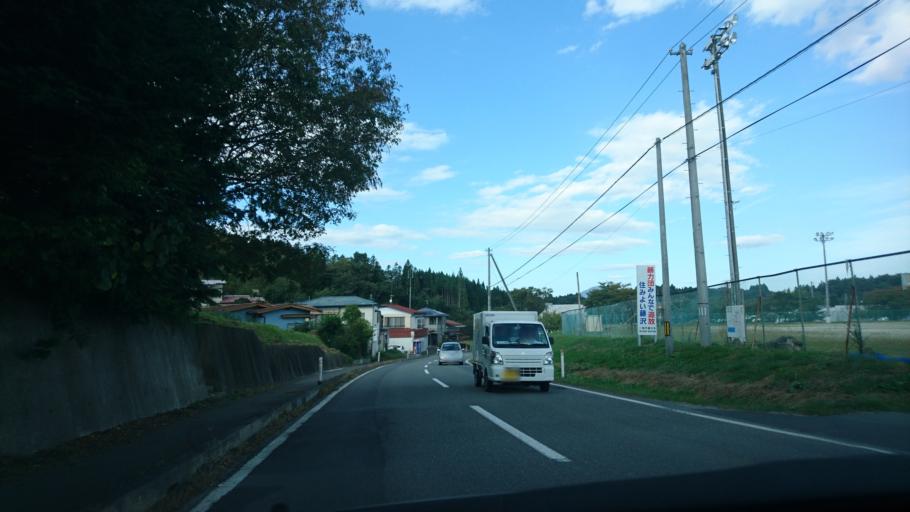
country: JP
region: Iwate
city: Ichinoseki
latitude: 38.8666
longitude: 141.3497
